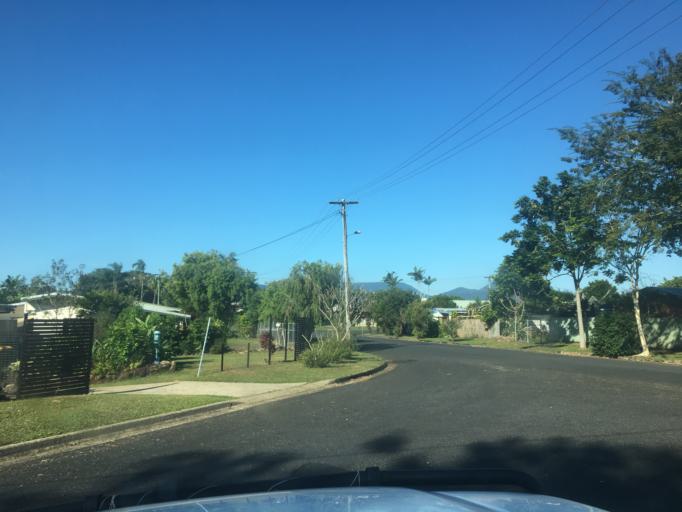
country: AU
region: Queensland
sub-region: Cairns
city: Woree
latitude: -16.9425
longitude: 145.7352
